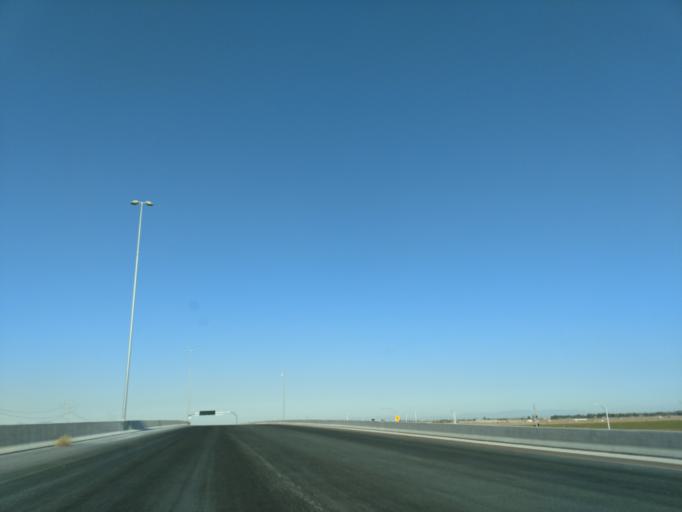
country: US
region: Arizona
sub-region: Maricopa County
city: Laveen
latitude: 33.3325
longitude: -112.1748
